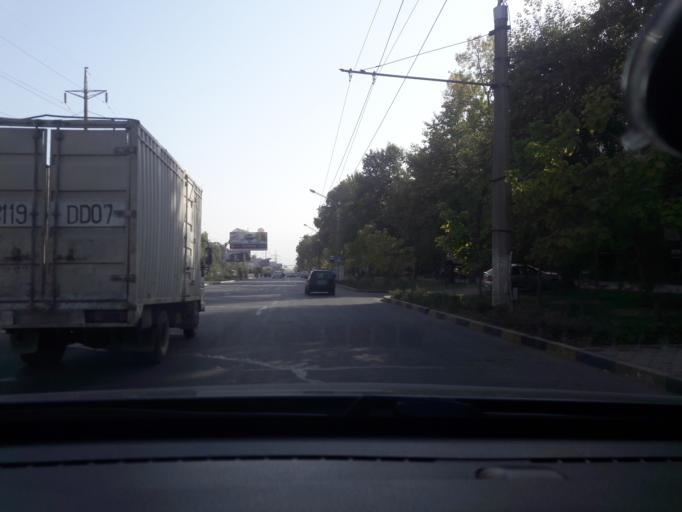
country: TJ
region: Dushanbe
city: Dushanbe
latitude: 38.5298
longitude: 68.7618
